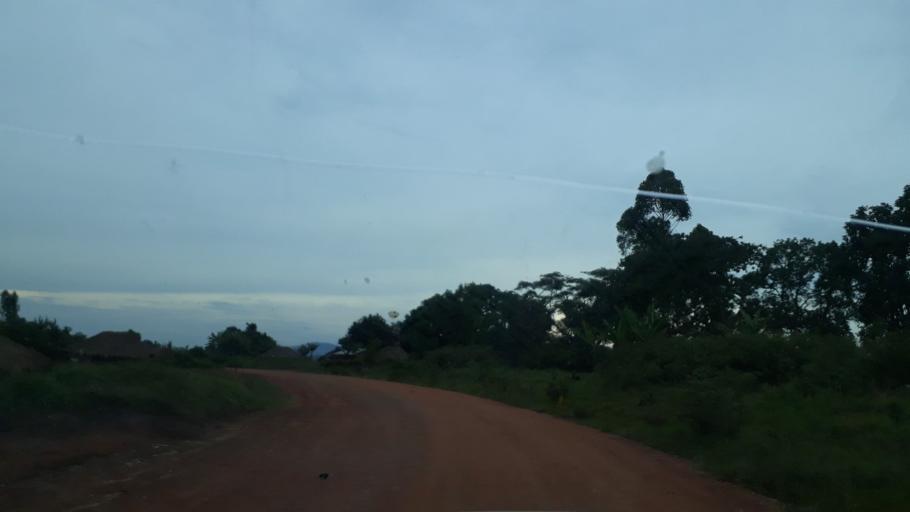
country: UG
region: Northern Region
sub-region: Zombo District
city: Paidha
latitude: 2.1753
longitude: 30.7161
